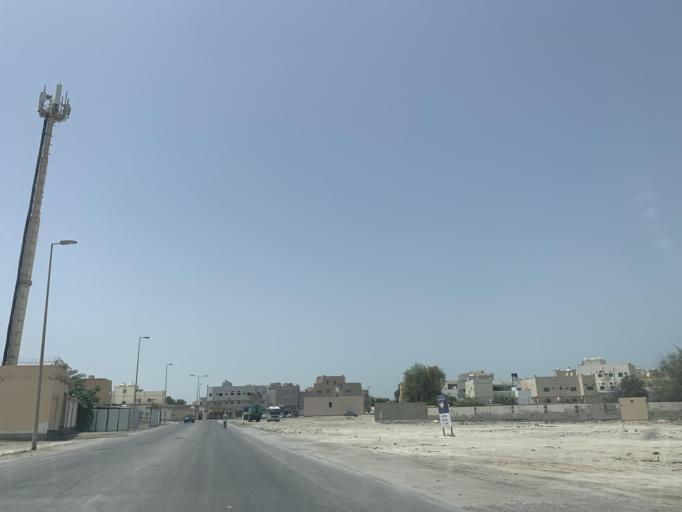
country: BH
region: Northern
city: Madinat `Isa
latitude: 26.1684
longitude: 50.5725
